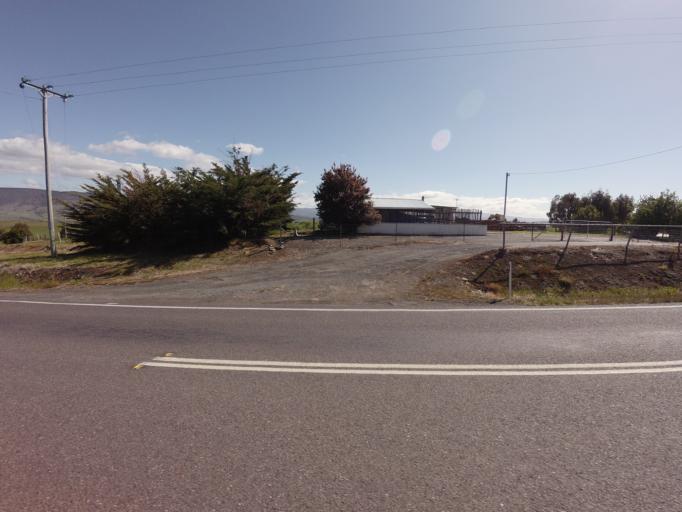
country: AU
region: Tasmania
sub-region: Derwent Valley
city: New Norfolk
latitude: -42.6987
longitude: 146.9434
